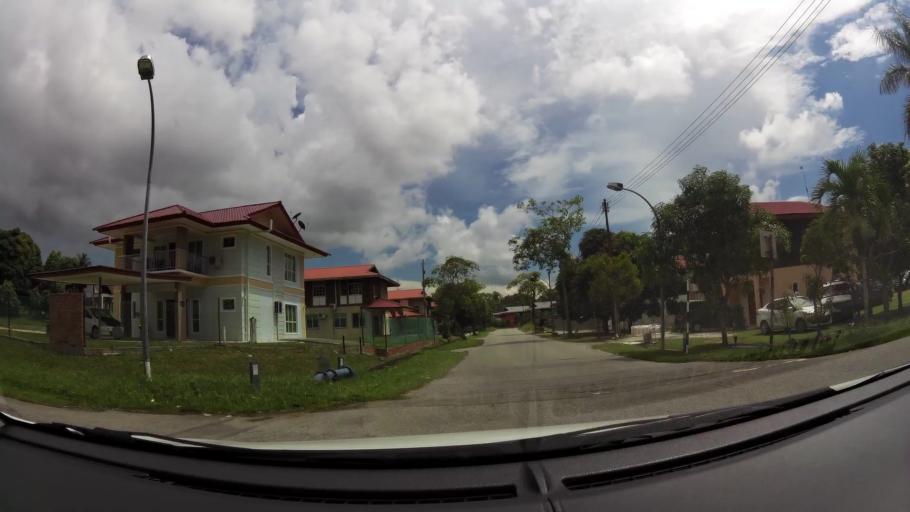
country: BN
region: Brunei and Muara
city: Bandar Seri Begawan
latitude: 4.9876
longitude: 114.9451
